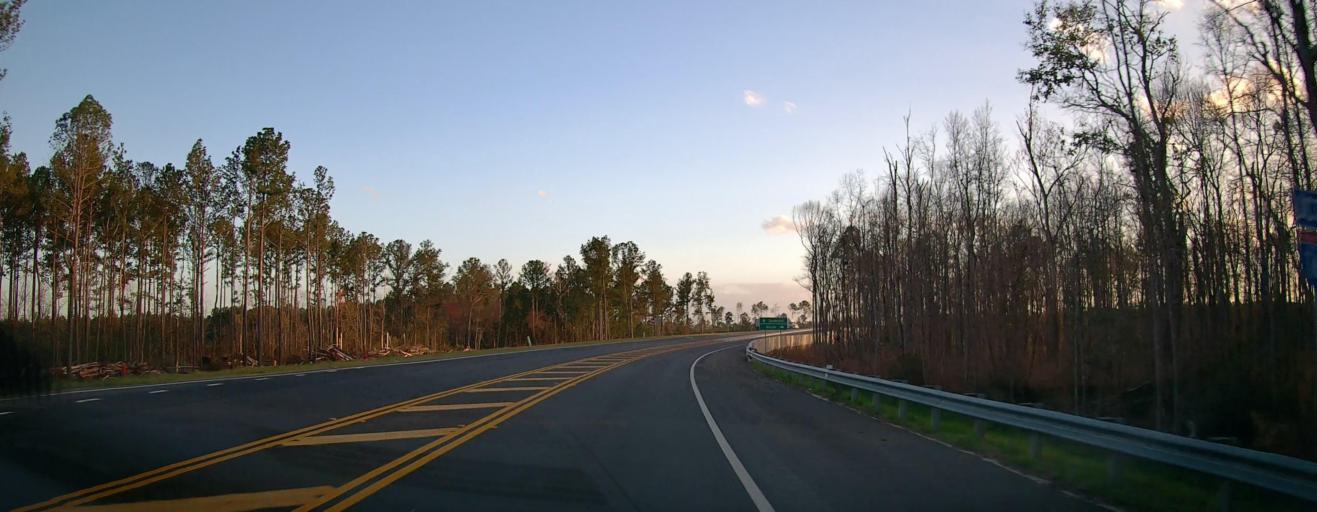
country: US
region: Georgia
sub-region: Chatham County
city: Bloomingdale
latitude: 32.1288
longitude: -81.3855
